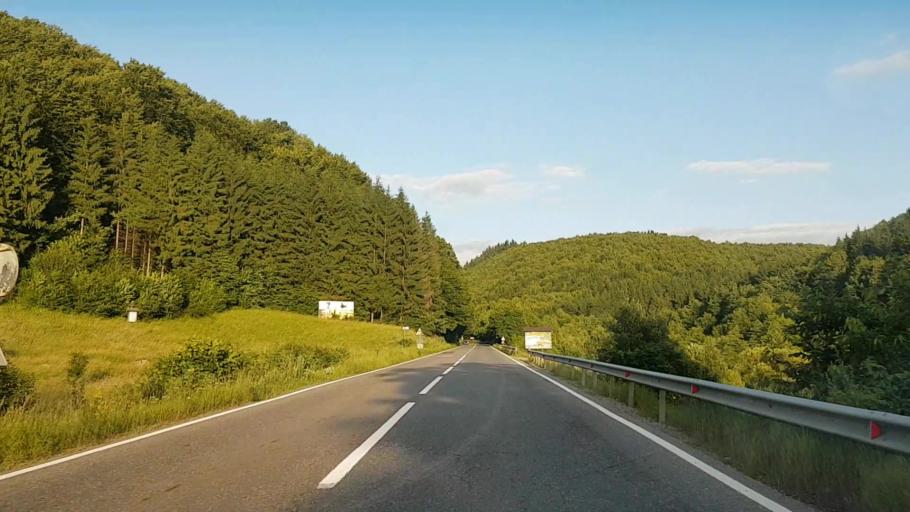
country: RO
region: Harghita
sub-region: Comuna Corund
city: Corund
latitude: 46.4508
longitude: 25.2144
